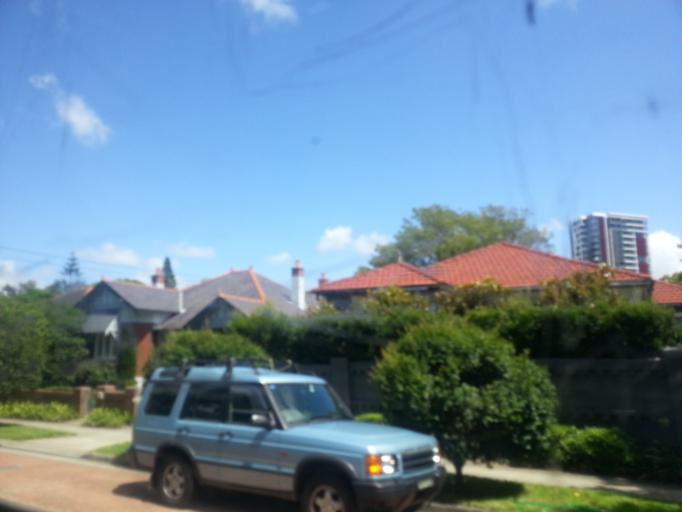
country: AU
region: New South Wales
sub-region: Randwick
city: Kensington
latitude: -33.9119
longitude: 151.2146
